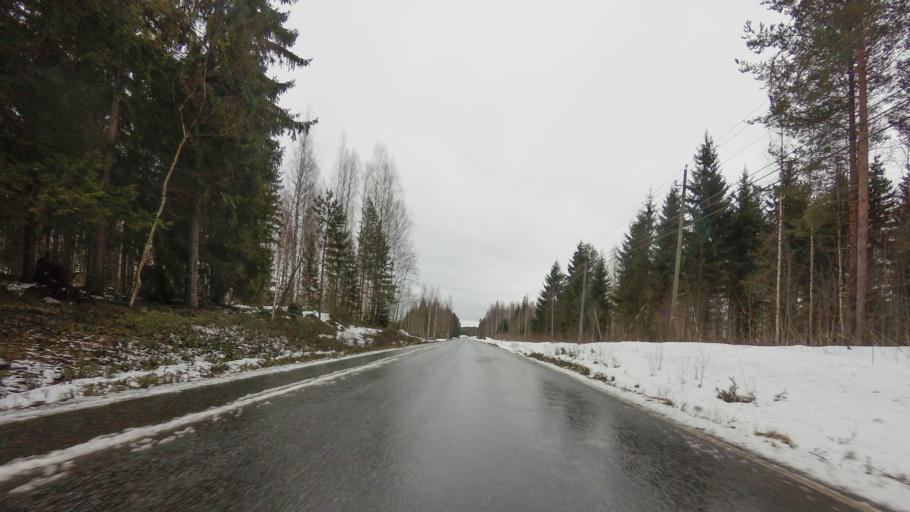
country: FI
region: Southern Savonia
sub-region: Savonlinna
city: Savonlinna
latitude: 61.9483
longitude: 28.8634
